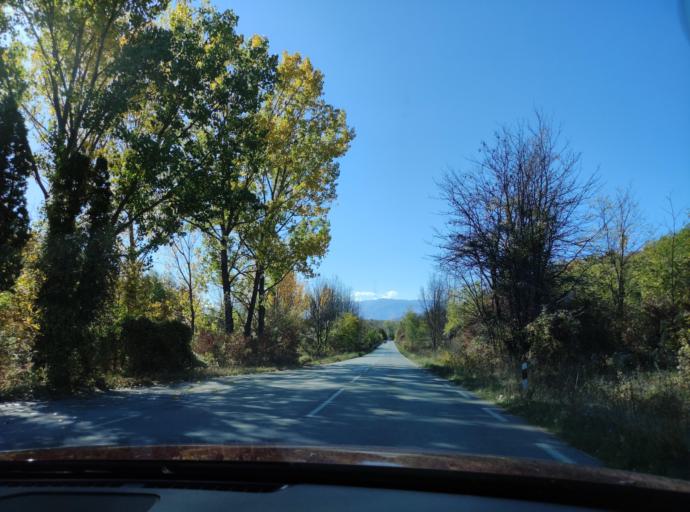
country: BG
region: Montana
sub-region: Obshtina Montana
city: Montana
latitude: 43.3997
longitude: 23.1298
